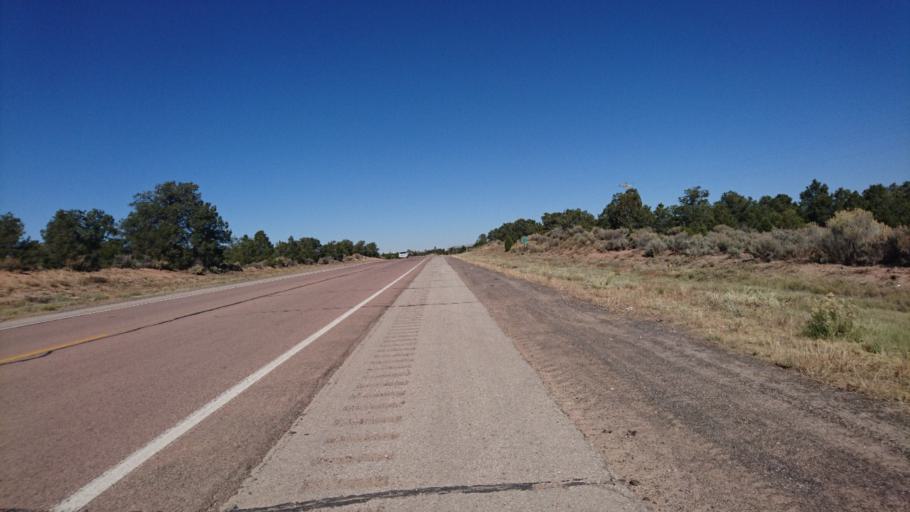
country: US
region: New Mexico
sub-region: McKinley County
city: Gallup
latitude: 35.3678
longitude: -108.7538
